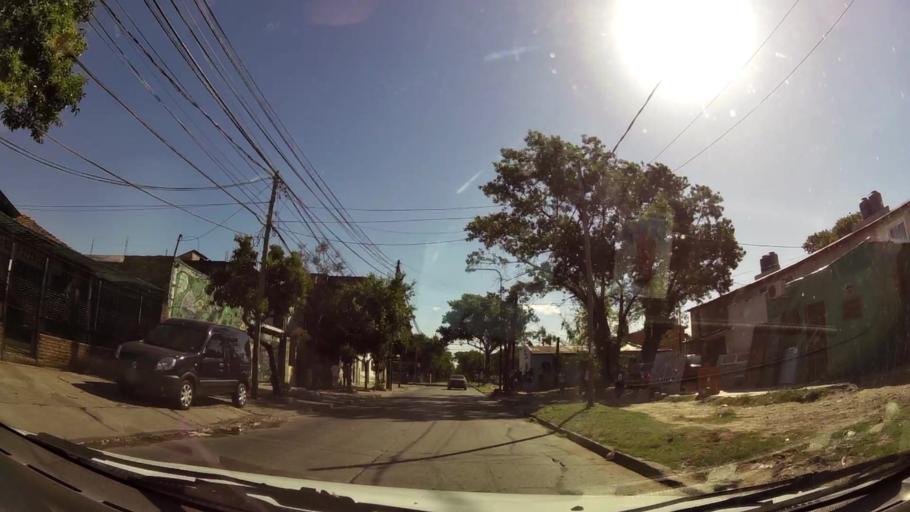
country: AR
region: Buenos Aires
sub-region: Partido de San Isidro
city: San Isidro
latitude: -34.4733
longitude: -58.5391
